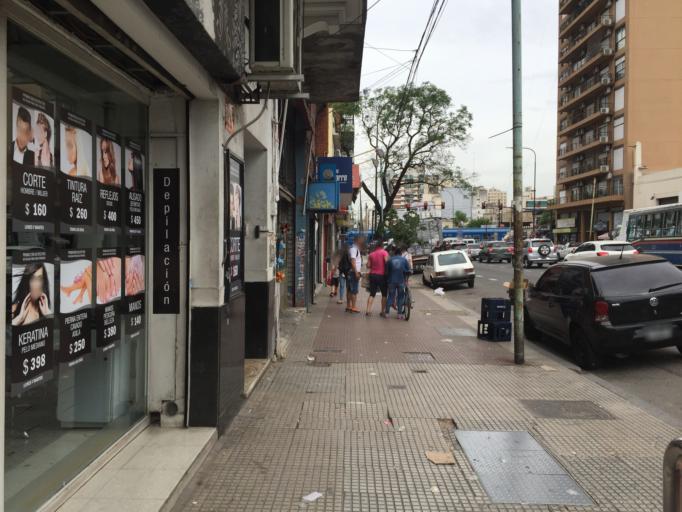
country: AR
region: Buenos Aires F.D.
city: Colegiales
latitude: -34.5917
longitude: -58.4475
